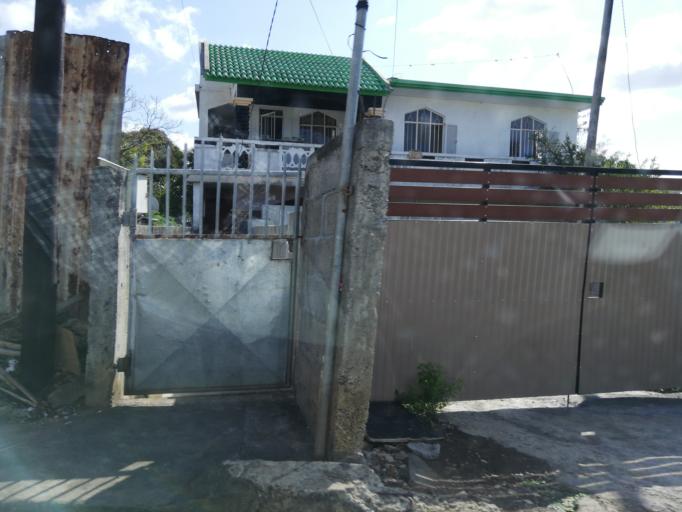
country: MU
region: Port Louis
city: Port Louis
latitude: -20.1653
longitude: 57.4828
